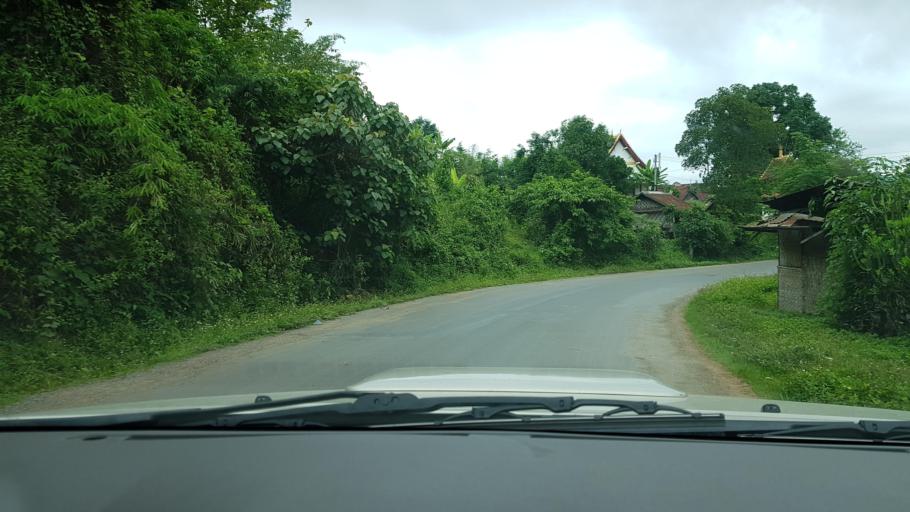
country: LA
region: Loungnamtha
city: Muang Nale
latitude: 20.3084
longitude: 101.6499
